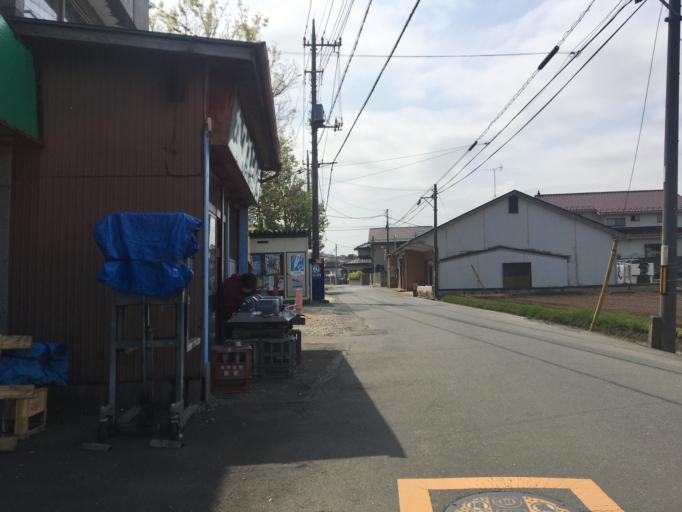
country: JP
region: Saitama
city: Kamifukuoka
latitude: 35.8884
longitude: 139.5260
